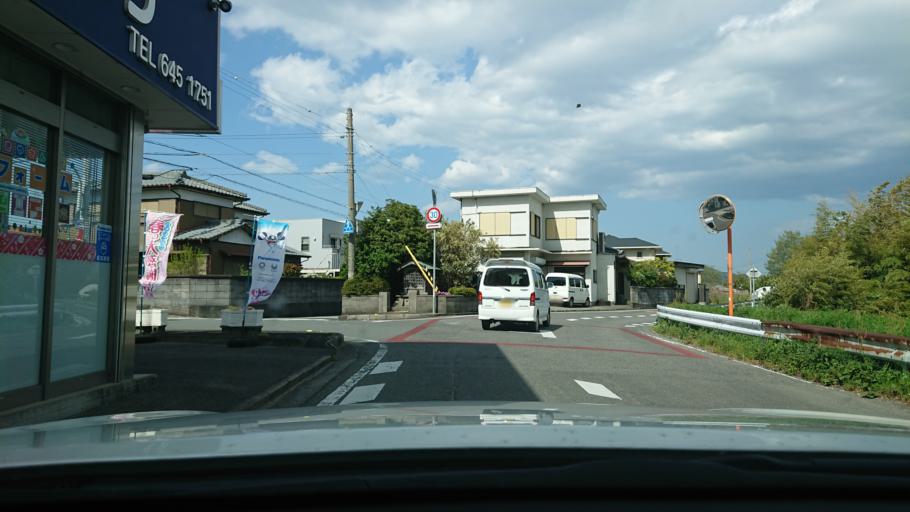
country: JP
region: Tokushima
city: Komatsushimacho
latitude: 34.0024
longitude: 134.5479
